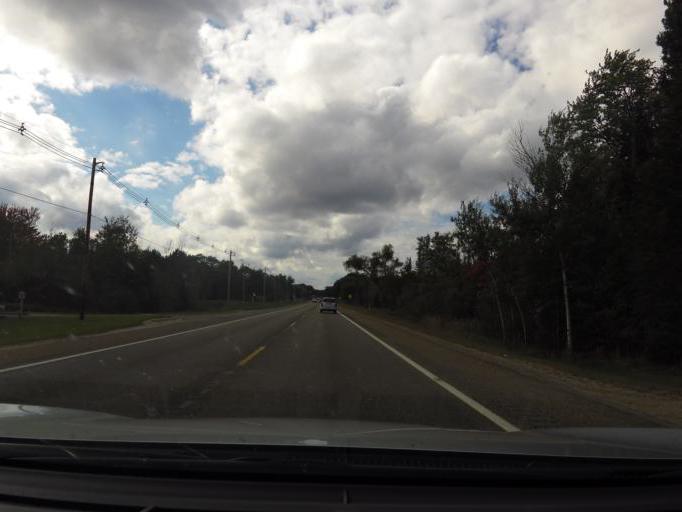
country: US
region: Michigan
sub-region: Roscommon County
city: Prudenville
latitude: 44.3055
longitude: -84.6275
